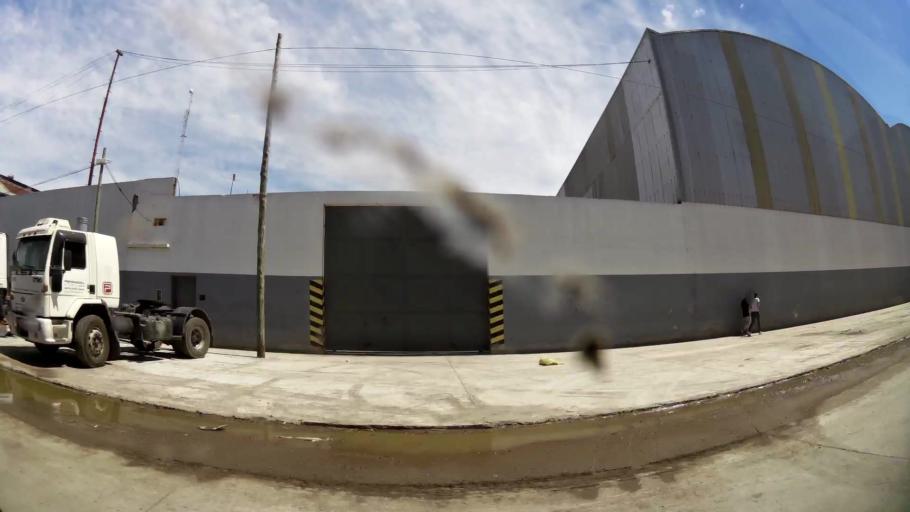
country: AR
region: Buenos Aires
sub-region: Partido de Quilmes
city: Quilmes
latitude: -34.7493
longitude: -58.3072
